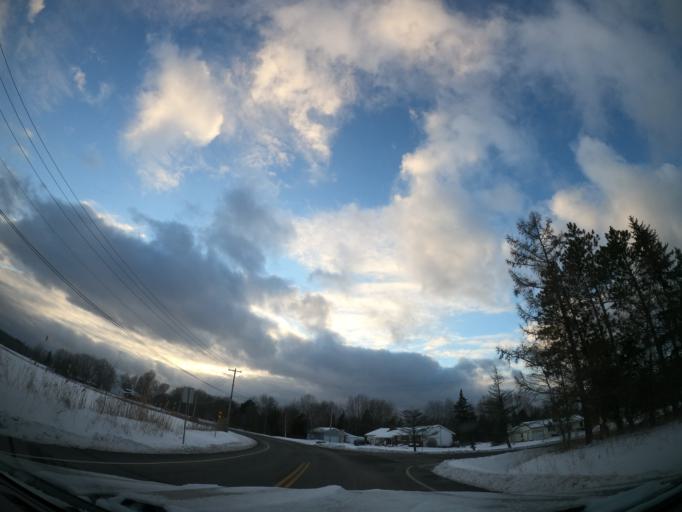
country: US
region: New York
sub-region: Onondaga County
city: Brewerton
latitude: 43.2164
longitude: -76.1511
